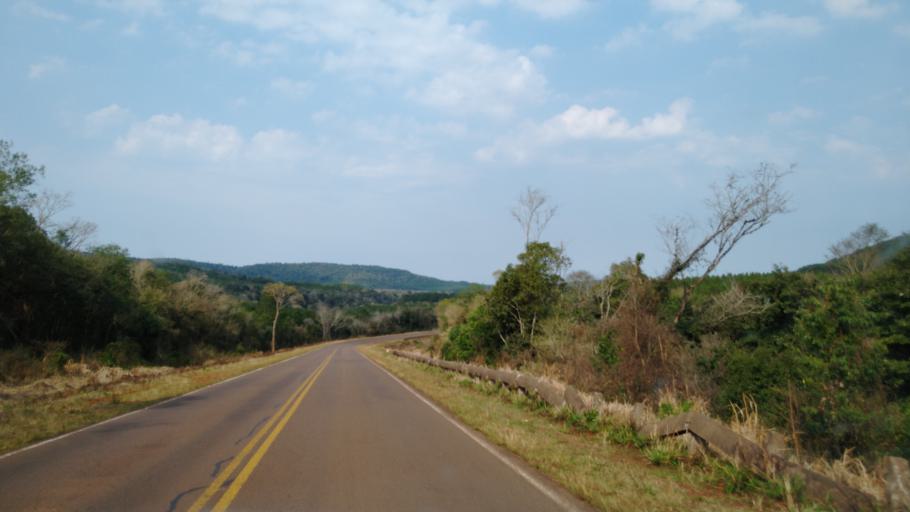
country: AR
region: Misiones
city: Santo Pipo
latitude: -27.2601
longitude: -55.2746
